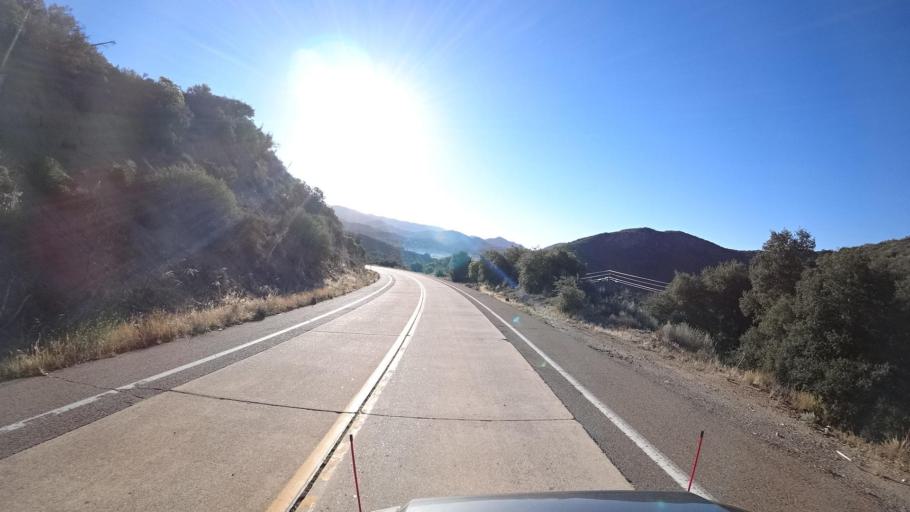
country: US
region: California
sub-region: San Diego County
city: Pine Valley
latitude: 32.8428
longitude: -116.5443
